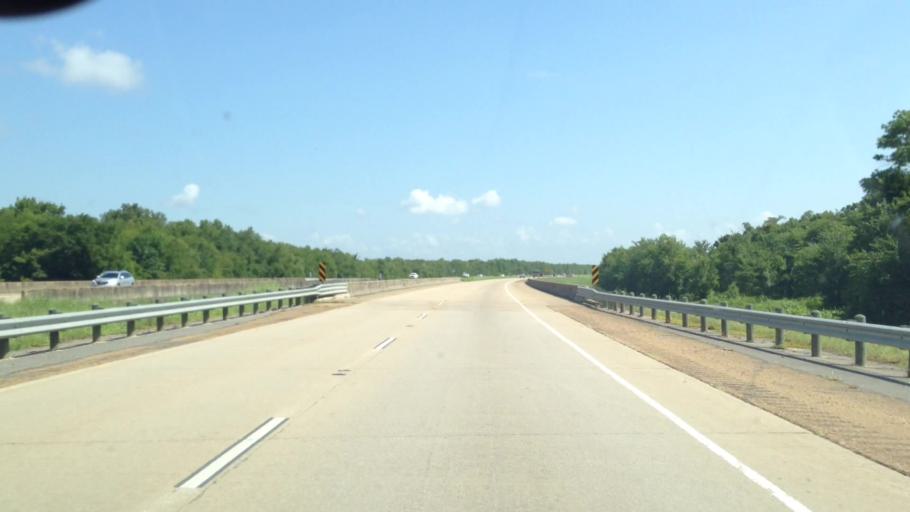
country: US
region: Louisiana
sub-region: Rapides Parish
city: Woodworth
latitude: 31.1975
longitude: -92.4741
